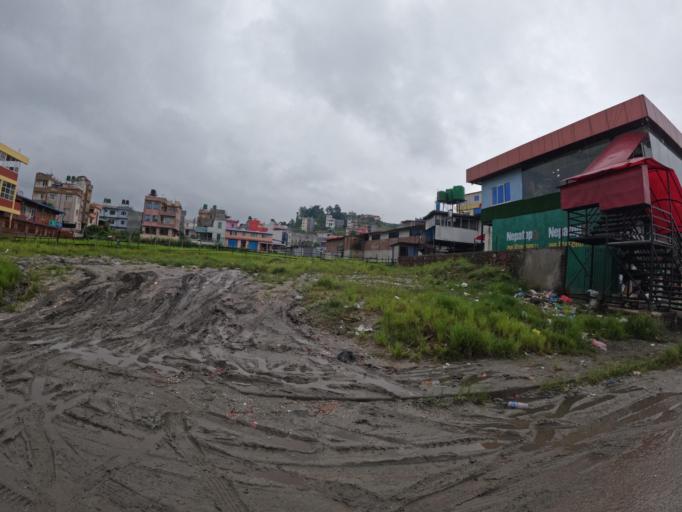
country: NP
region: Central Region
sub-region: Bagmati Zone
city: Kathmandu
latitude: 27.7620
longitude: 85.3173
